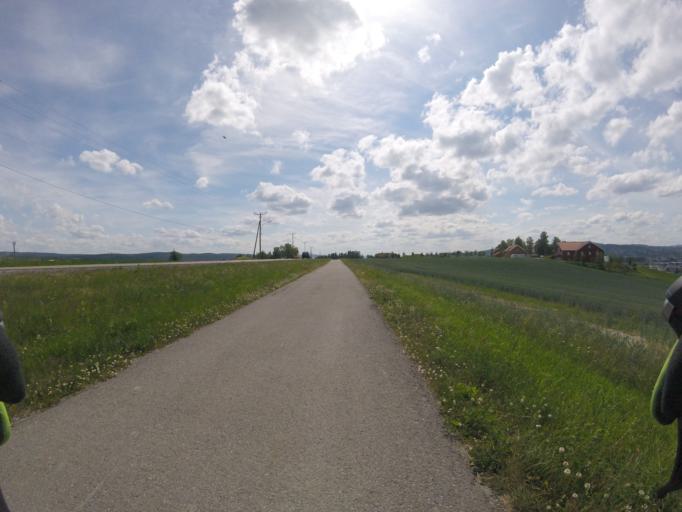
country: NO
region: Akershus
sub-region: Skedsmo
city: Lillestrom
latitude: 59.9813
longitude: 11.0526
